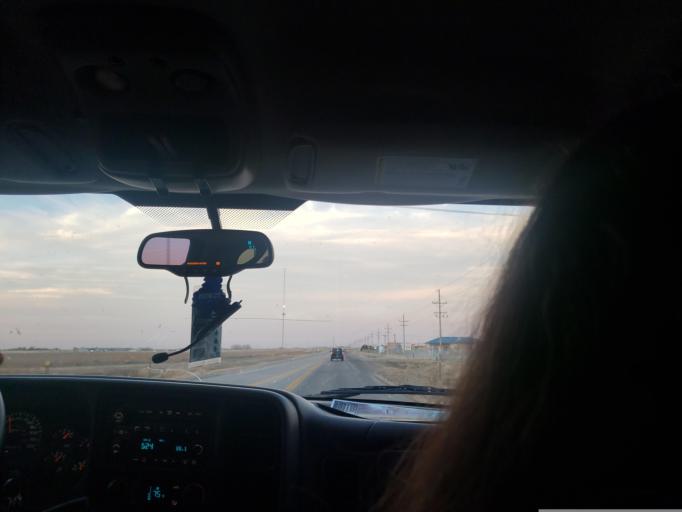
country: US
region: Kansas
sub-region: Seward County
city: Liberal
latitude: 37.0537
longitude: -100.9042
